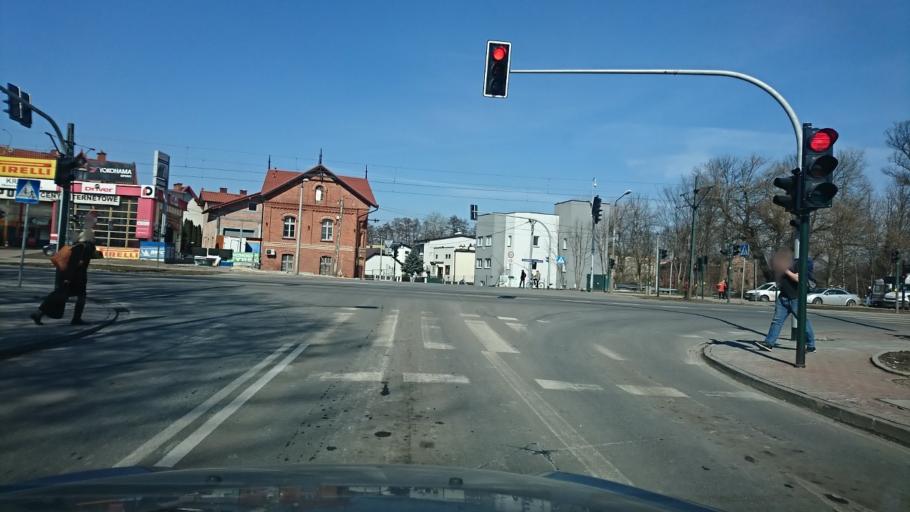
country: PL
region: Lesser Poland Voivodeship
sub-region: Powiat wielicki
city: Kokotow
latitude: 50.0850
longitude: 20.0385
